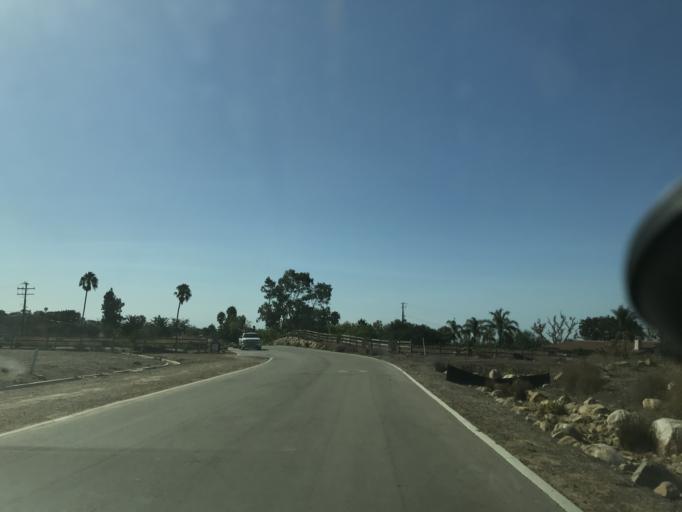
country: US
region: California
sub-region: Santa Barbara County
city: Goleta
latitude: 34.4576
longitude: -119.7864
